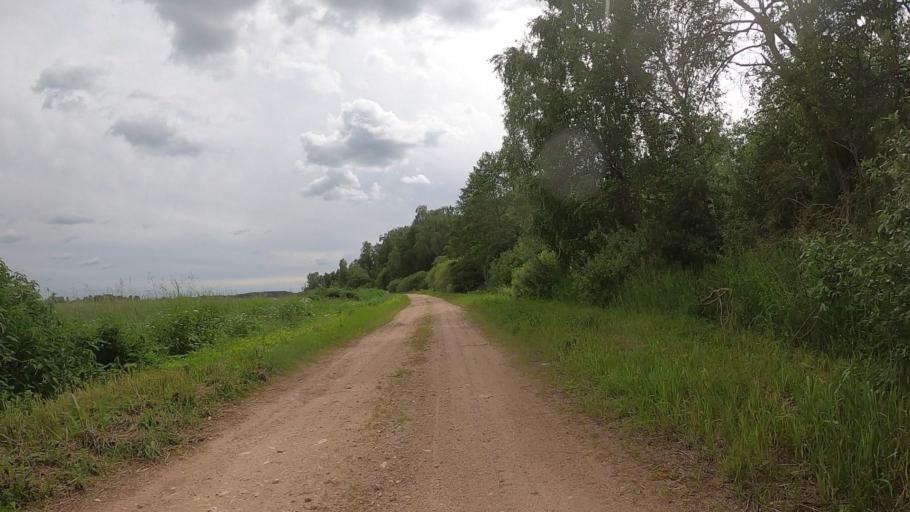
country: LV
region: Olaine
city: Olaine
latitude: 56.8219
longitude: 23.9379
